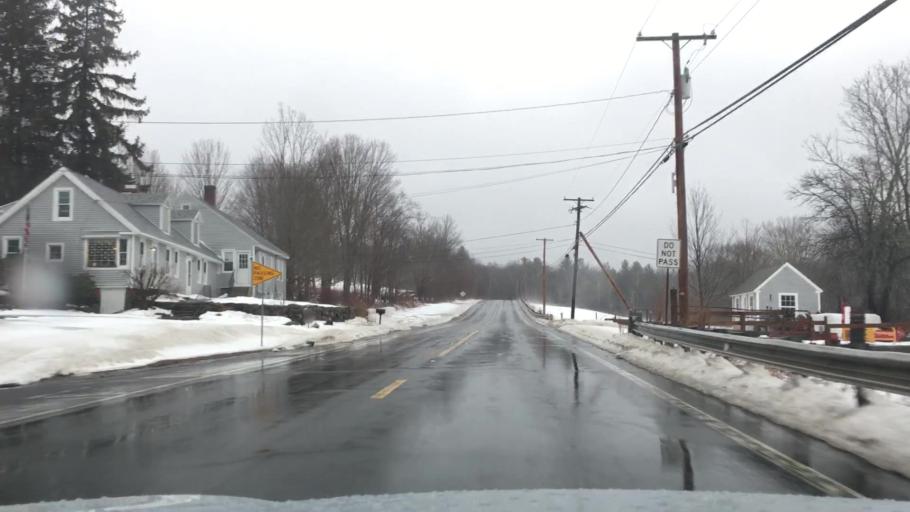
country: US
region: Massachusetts
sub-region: Hampshire County
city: Belchertown
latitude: 42.3111
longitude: -72.4065
